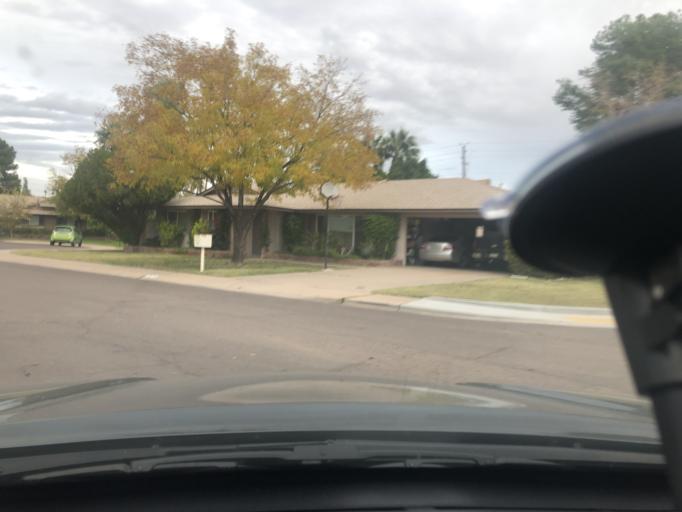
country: US
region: Arizona
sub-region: Maricopa County
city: Scottsdale
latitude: 33.4840
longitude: -111.8967
